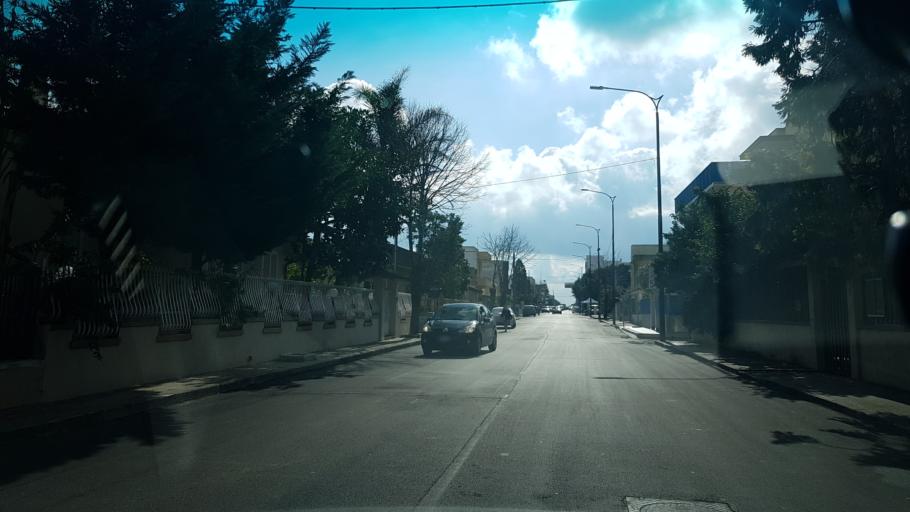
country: IT
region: Apulia
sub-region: Provincia di Brindisi
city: San Pietro Vernotico
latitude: 40.4811
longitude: 18.0047
